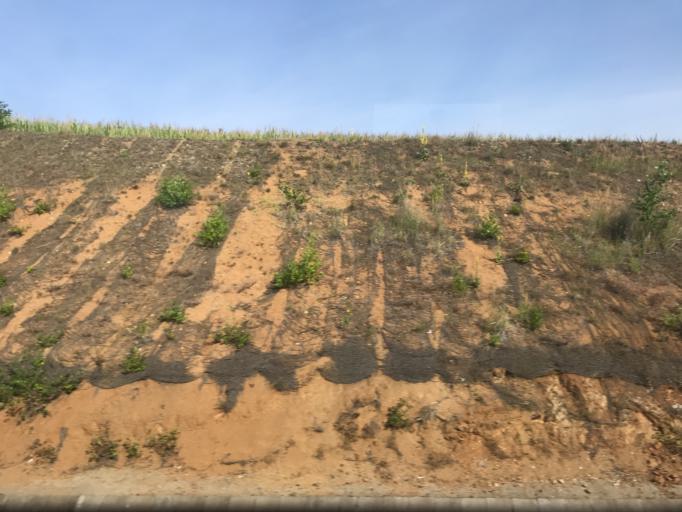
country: CZ
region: Central Bohemia
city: Bystrice
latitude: 49.7001
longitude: 14.6570
